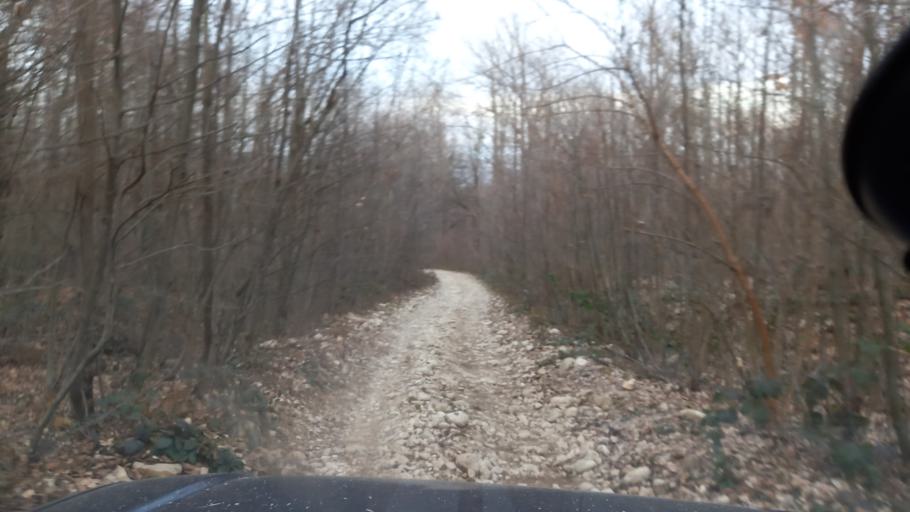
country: RU
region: Krasnodarskiy
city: Neftegorsk
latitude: 44.2264
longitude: 39.8969
